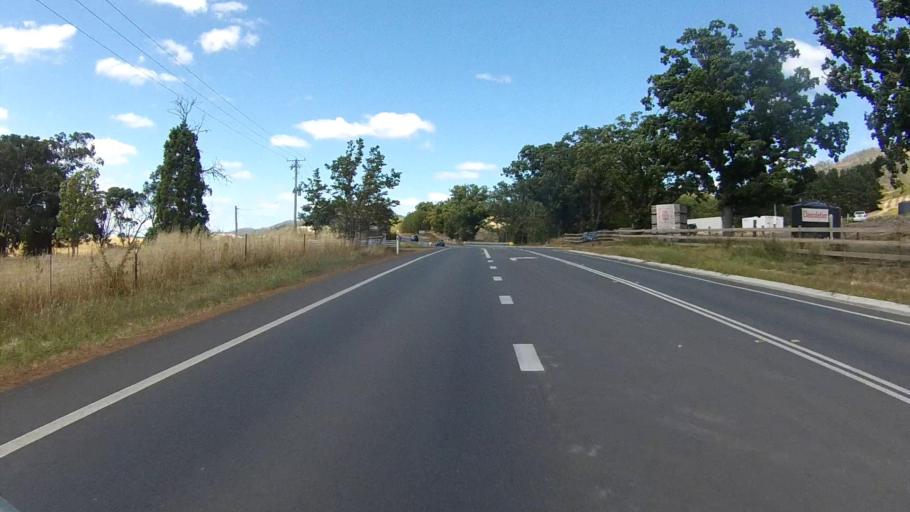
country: AU
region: Tasmania
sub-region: Clarence
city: Cambridge
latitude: -42.8032
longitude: 147.4228
